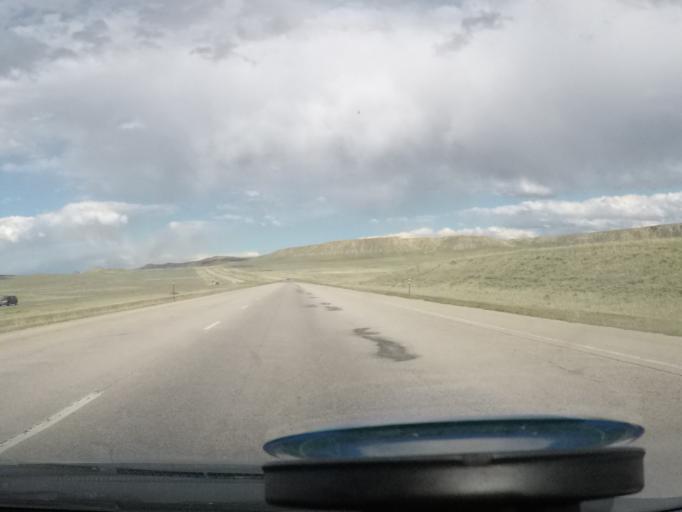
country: US
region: Wyoming
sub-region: Converse County
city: Glenrock
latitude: 42.8355
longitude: -105.9925
